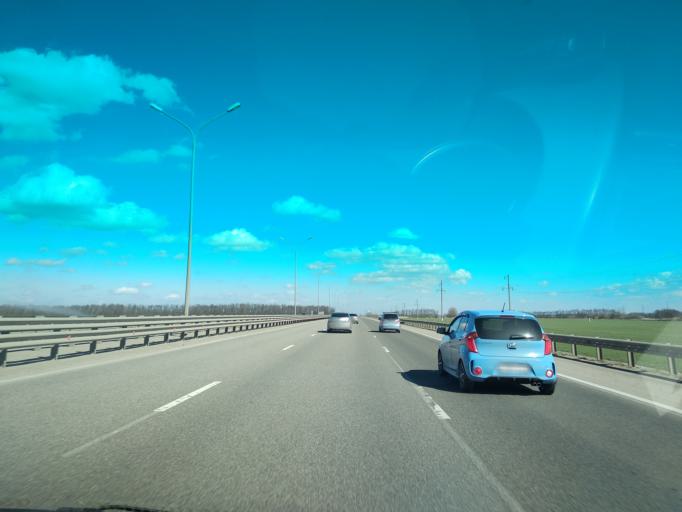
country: RU
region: Krasnodarskiy
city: Agronom
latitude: 45.2004
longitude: 39.1447
